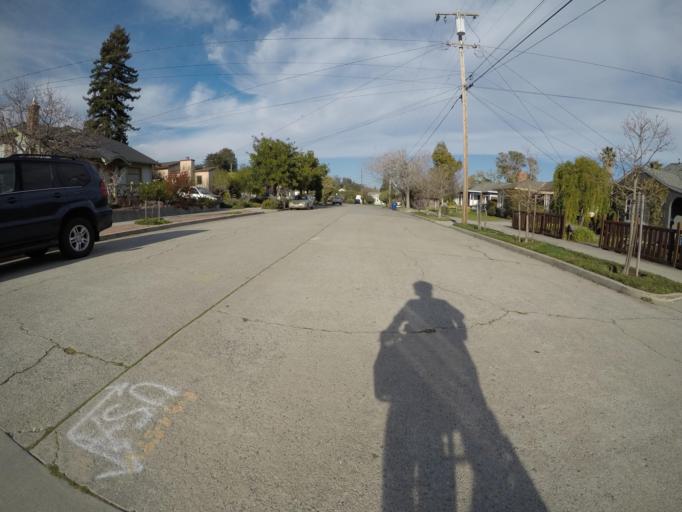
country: US
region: California
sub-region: Santa Cruz County
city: Santa Cruz
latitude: 36.9695
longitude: -122.0433
